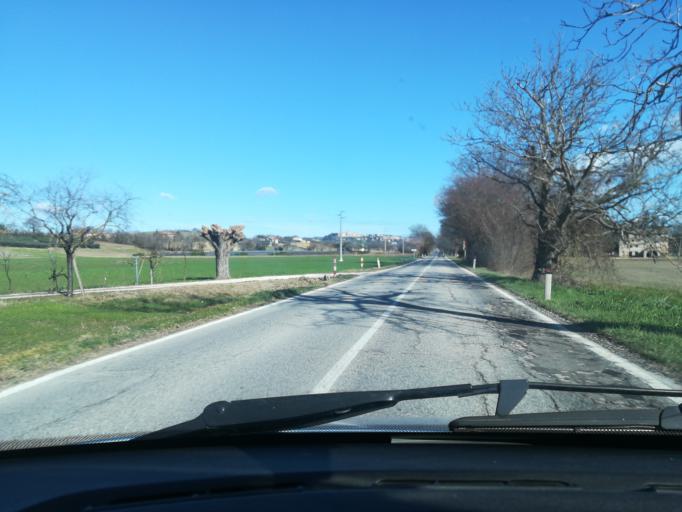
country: IT
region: The Marches
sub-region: Provincia di Macerata
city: Villa Potenza
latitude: 43.3330
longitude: 13.4264
